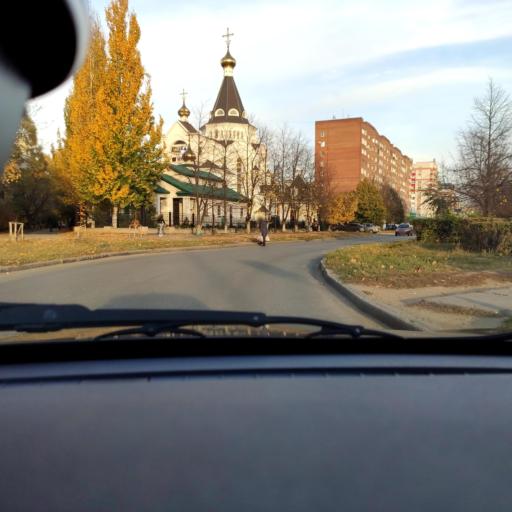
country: RU
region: Samara
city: Tol'yatti
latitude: 53.5424
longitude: 49.3328
